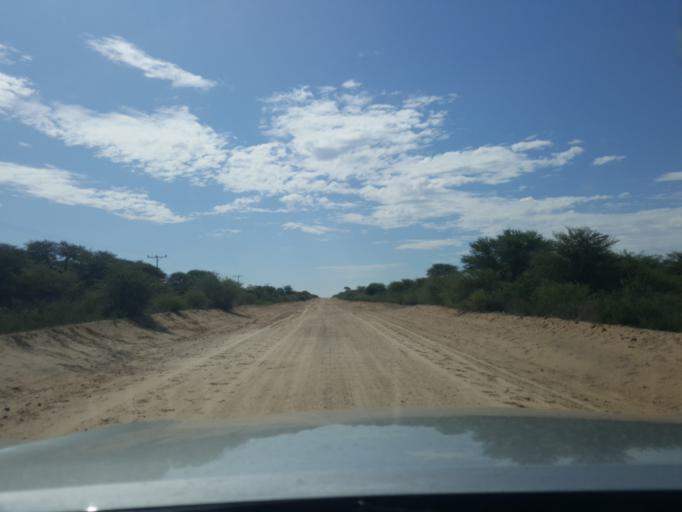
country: BW
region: Kweneng
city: Khudumelapye
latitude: -23.8773
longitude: 24.9036
